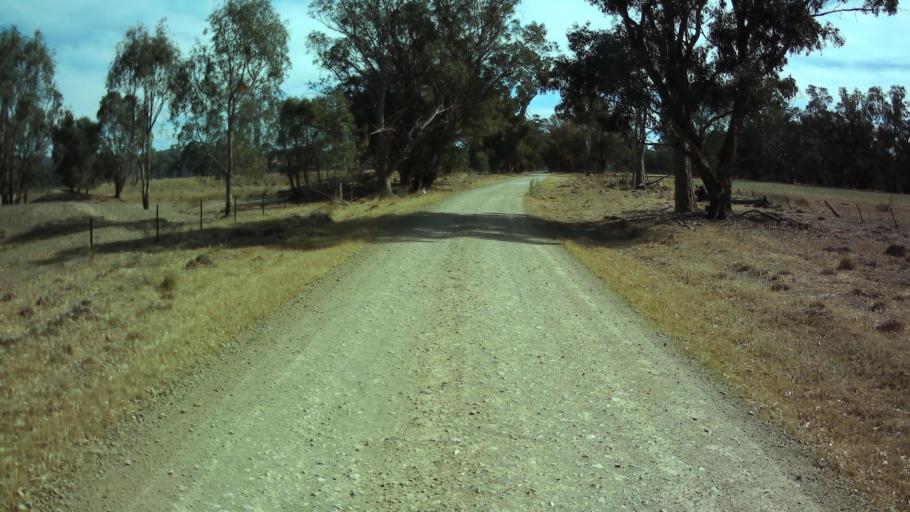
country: AU
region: New South Wales
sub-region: Weddin
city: Grenfell
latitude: -33.6914
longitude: 148.3039
